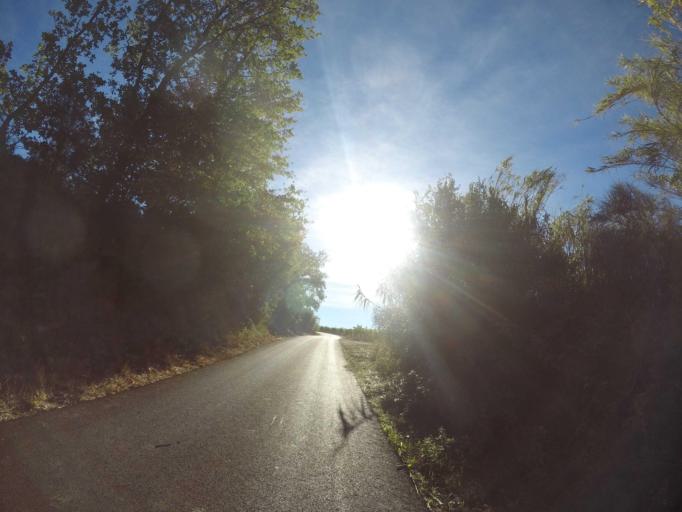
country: FR
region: Languedoc-Roussillon
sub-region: Departement des Pyrenees-Orientales
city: Trouillas
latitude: 42.5699
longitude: 2.7929
